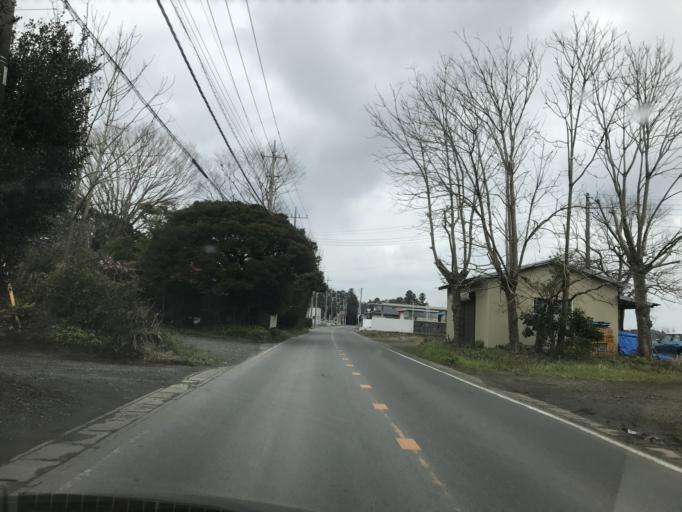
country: JP
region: Chiba
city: Sawara
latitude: 35.8421
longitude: 140.5062
